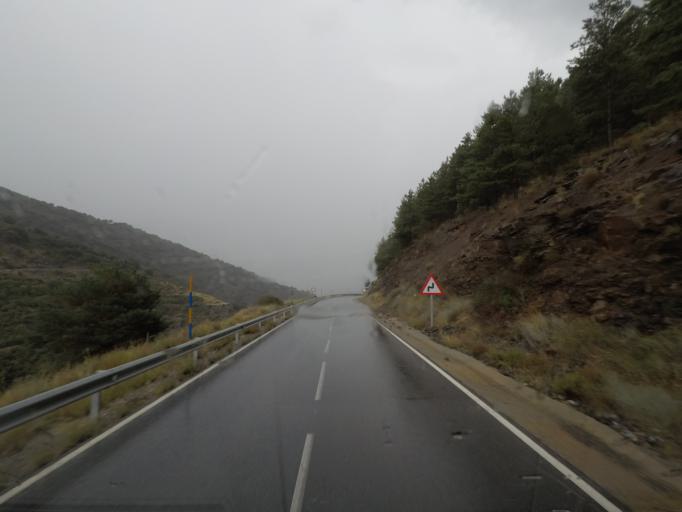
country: ES
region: Andalusia
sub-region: Provincia de Almeria
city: Bayarcal
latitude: 37.0680
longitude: -3.0172
